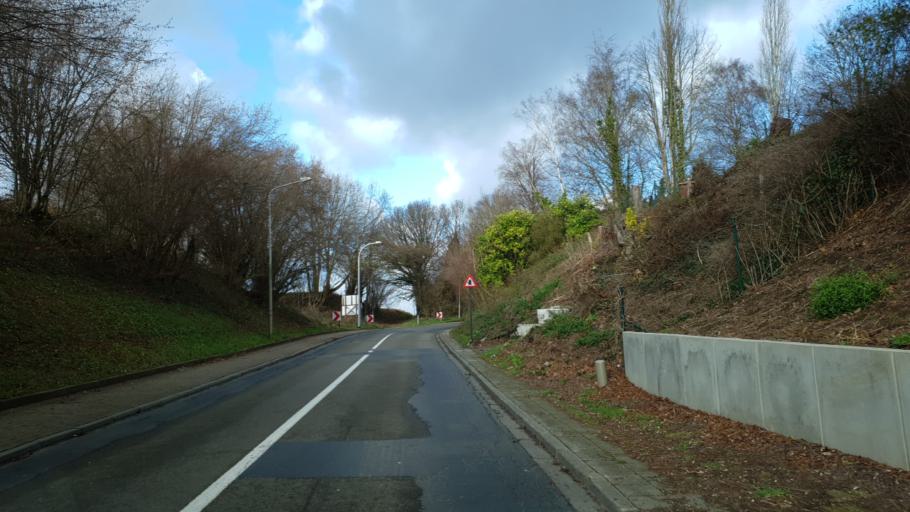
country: BE
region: Flanders
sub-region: Provincie Vlaams-Brabant
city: Tervuren
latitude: 50.8423
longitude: 4.5363
